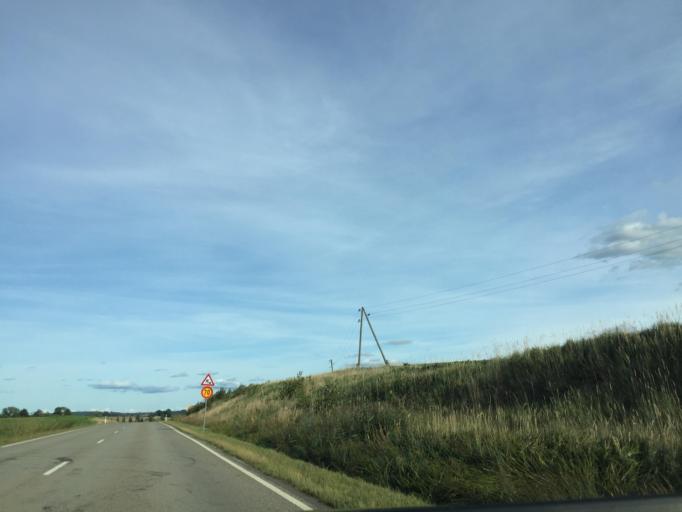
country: LV
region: Kandava
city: Kandava
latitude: 56.9081
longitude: 22.9200
